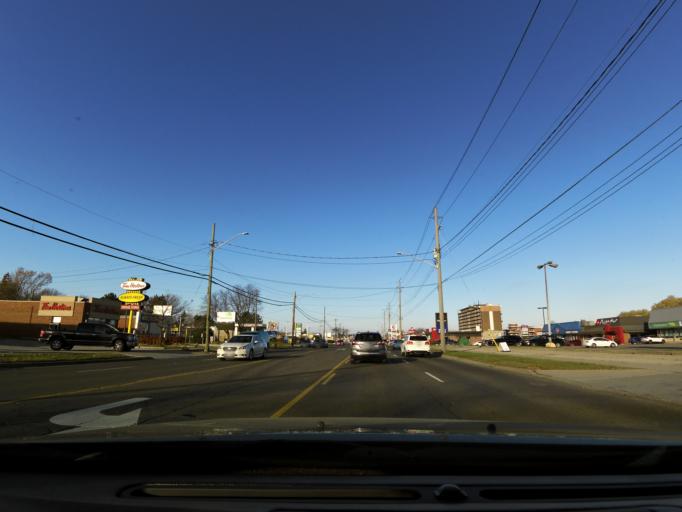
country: CA
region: Ontario
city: Hamilton
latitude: 43.2257
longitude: -79.8829
